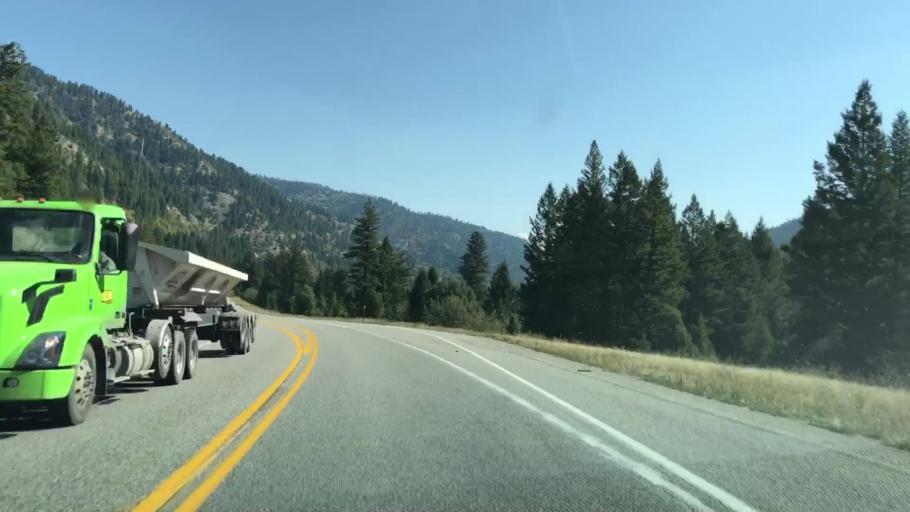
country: US
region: Wyoming
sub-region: Teton County
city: Hoback
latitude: 43.1828
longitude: -110.9609
